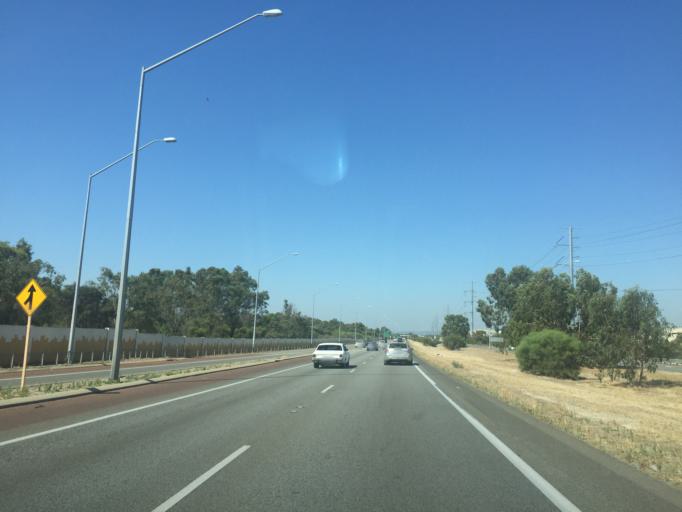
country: AU
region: Western Australia
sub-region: Canning
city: Willetton
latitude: -32.0660
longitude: 115.8934
